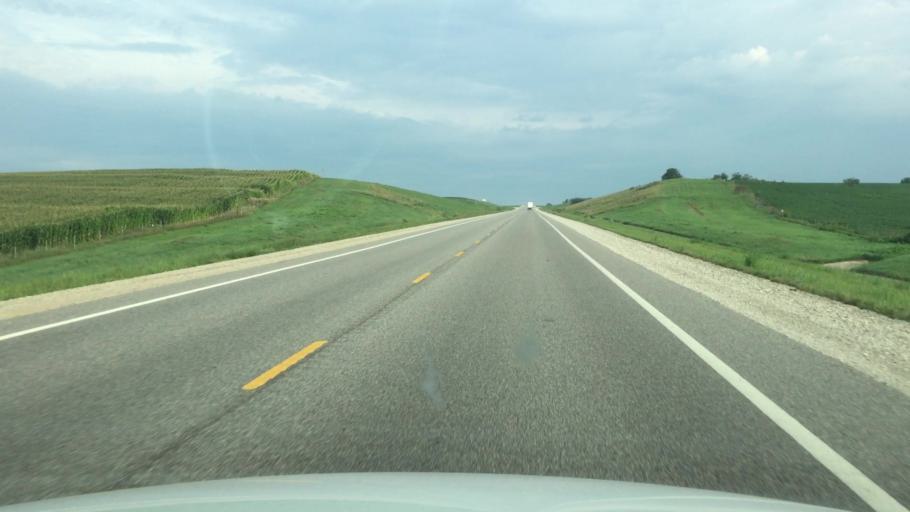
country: US
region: Kansas
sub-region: Doniphan County
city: Highland
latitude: 39.8213
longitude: -95.2123
